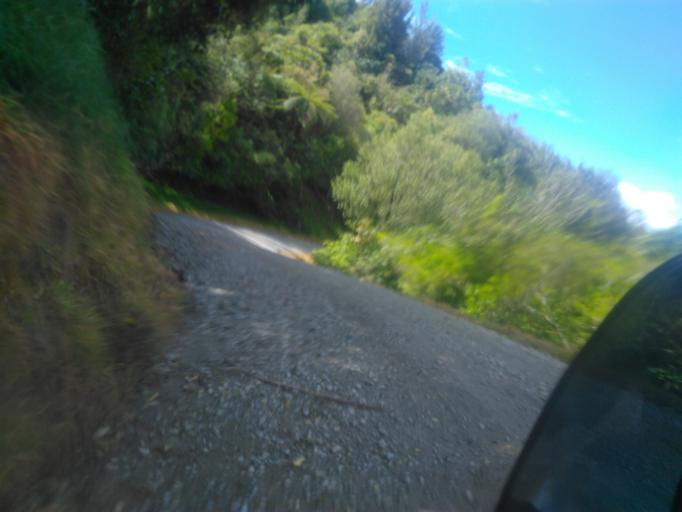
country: NZ
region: Hawke's Bay
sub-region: Wairoa District
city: Wairoa
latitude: -38.7769
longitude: 177.6237
